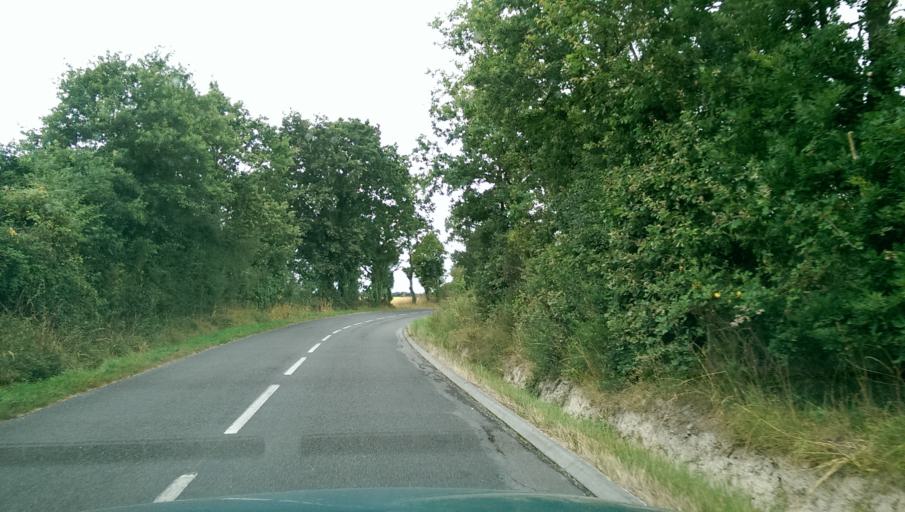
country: FR
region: Pays de la Loire
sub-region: Departement de la Loire-Atlantique
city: La Planche
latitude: 47.0015
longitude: -1.3986
